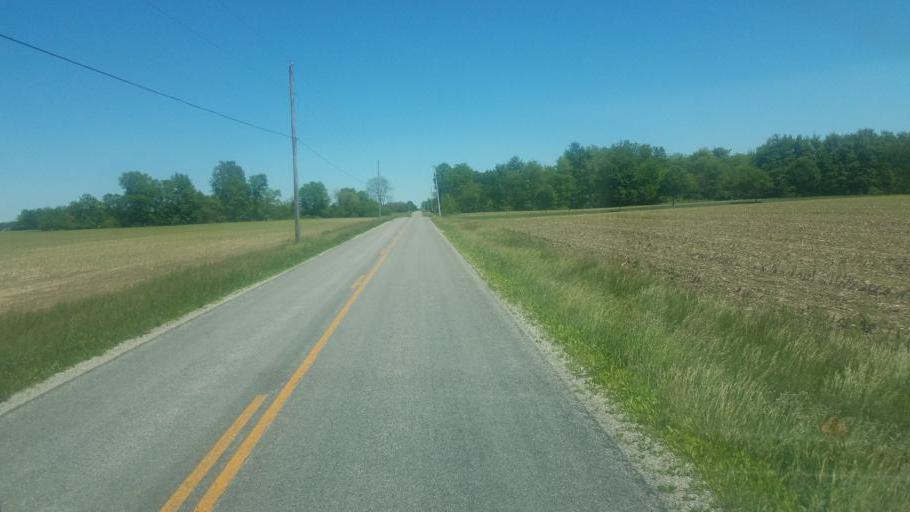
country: US
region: Ohio
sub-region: Shelby County
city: Sidney
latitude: 40.2134
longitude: -84.1521
